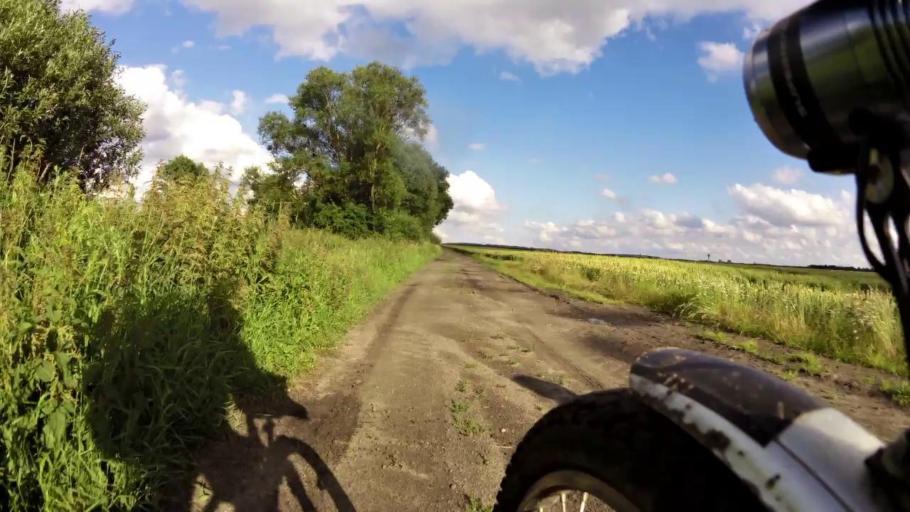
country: PL
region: West Pomeranian Voivodeship
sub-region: Powiat swidwinski
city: Swidwin
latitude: 53.7702
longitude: 15.8650
